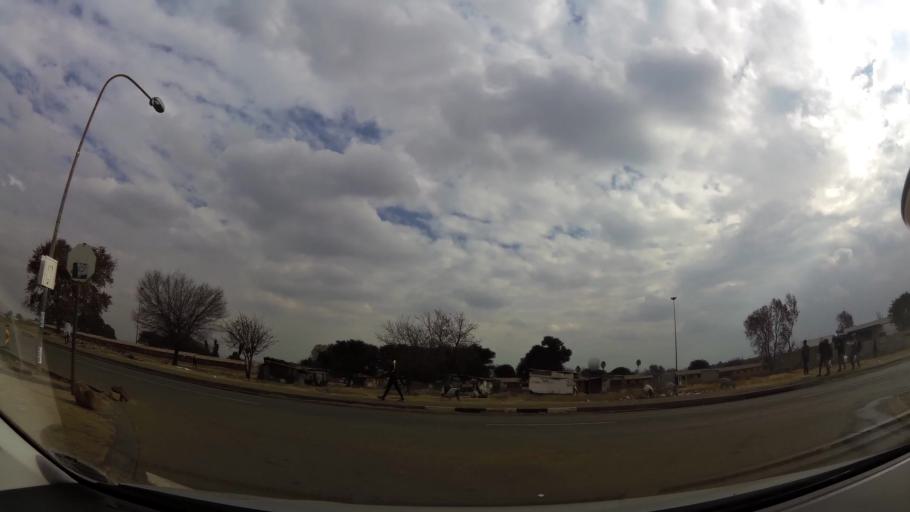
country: ZA
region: Gauteng
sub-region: City of Johannesburg Metropolitan Municipality
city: Soweto
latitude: -26.2639
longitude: 27.8483
